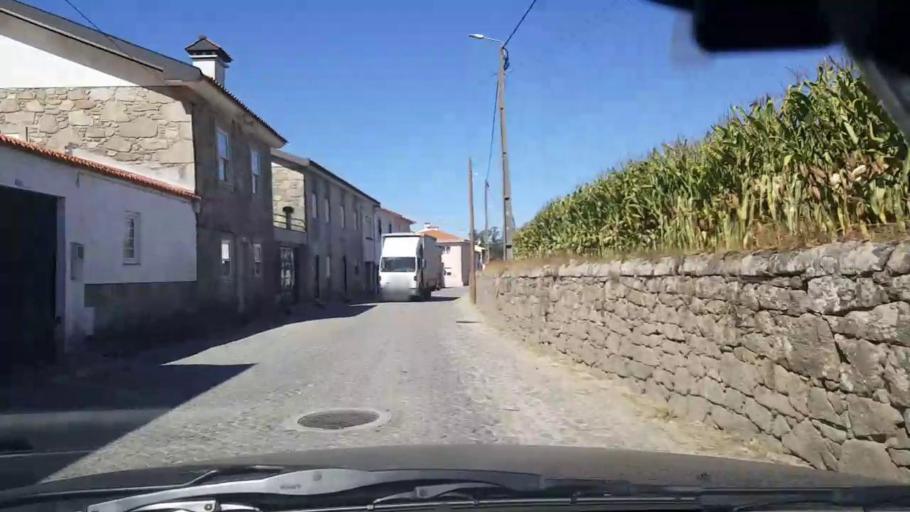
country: PT
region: Porto
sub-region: Vila do Conde
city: Arvore
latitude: 41.3249
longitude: -8.7048
